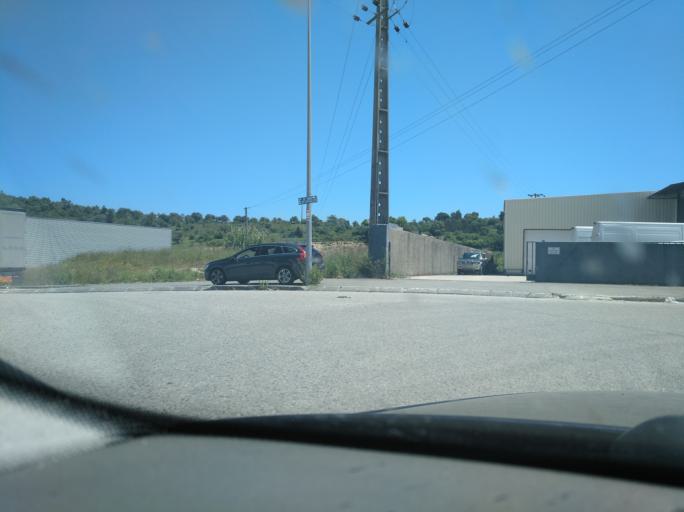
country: PT
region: Coimbra
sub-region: Coimbra
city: Coimbra
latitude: 40.2382
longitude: -8.4340
